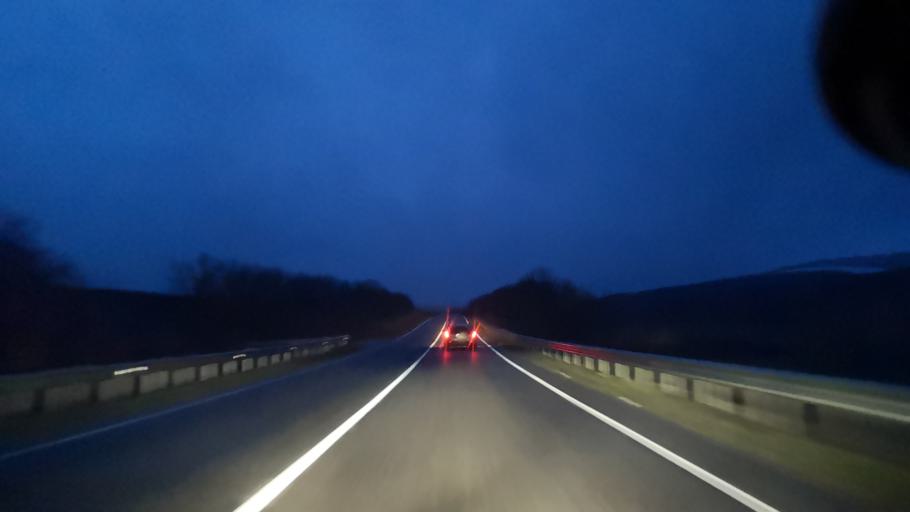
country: MD
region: Orhei
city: Orhei
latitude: 47.4847
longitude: 28.7915
